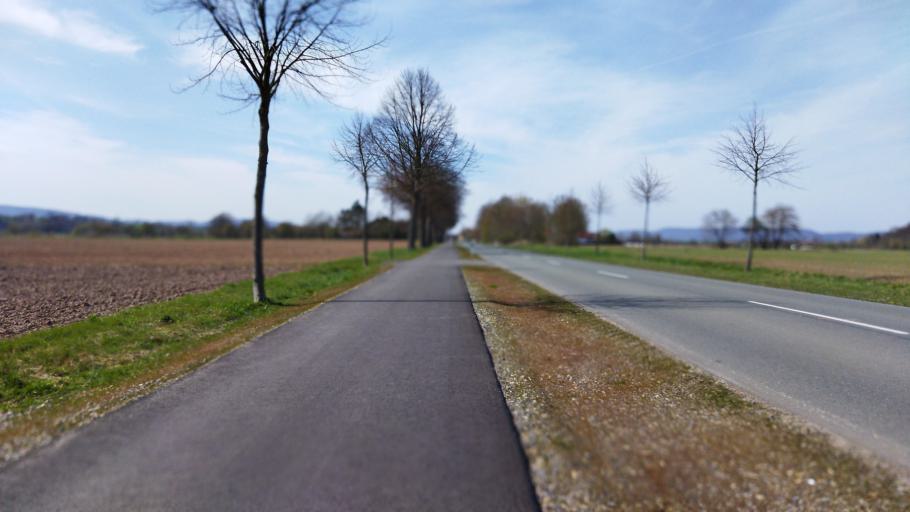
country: DE
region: Lower Saxony
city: Hameln
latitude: 52.1223
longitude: 9.3156
